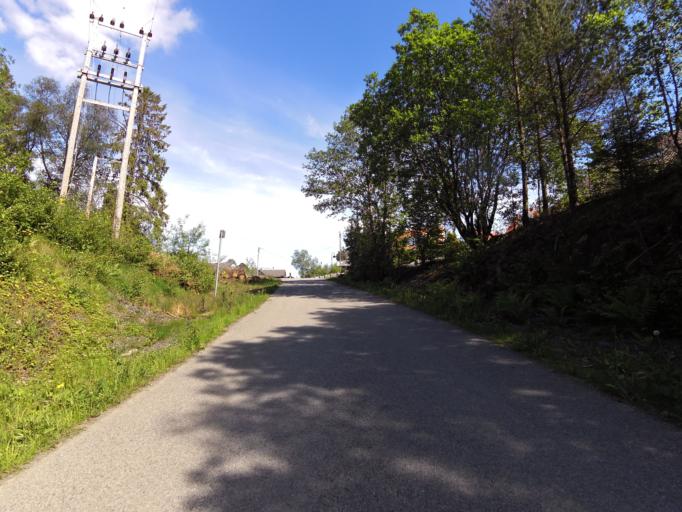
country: NO
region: Hordaland
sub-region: Stord
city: Leirvik
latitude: 59.7877
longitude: 5.4902
